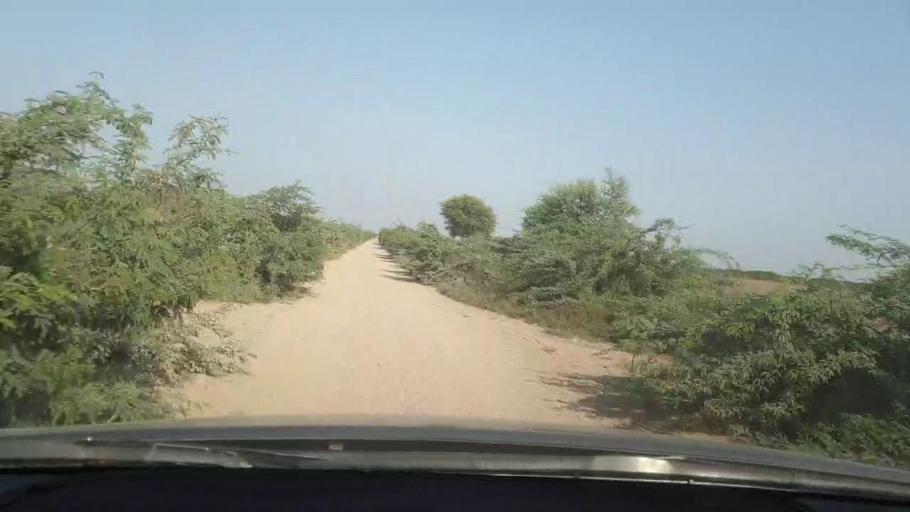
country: PK
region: Sindh
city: Naukot
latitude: 24.7781
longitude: 69.2748
